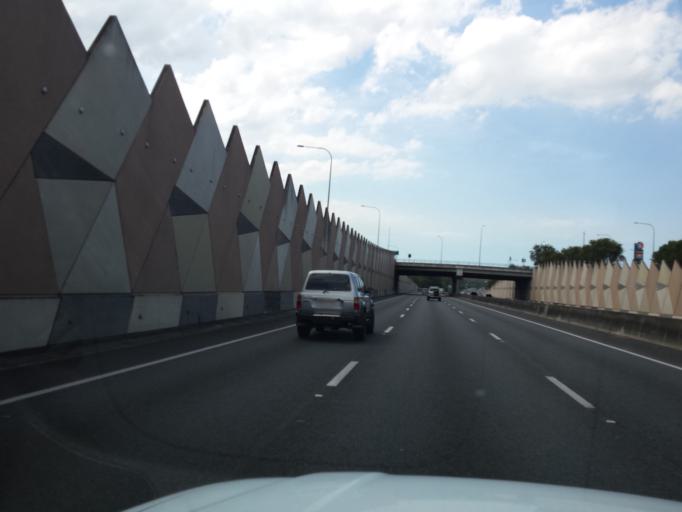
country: AU
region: Queensland
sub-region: Gold Coast
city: Nerang
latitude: -27.9952
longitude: 153.3400
